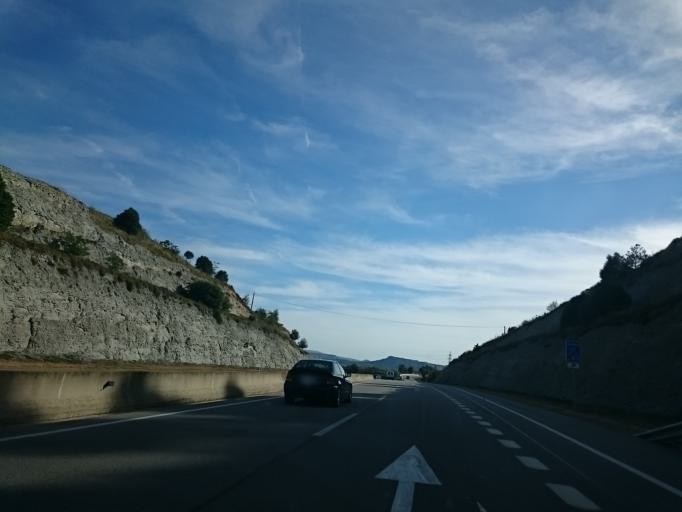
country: ES
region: Catalonia
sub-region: Provincia de Barcelona
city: Gurb
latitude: 41.9310
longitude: 2.2301
